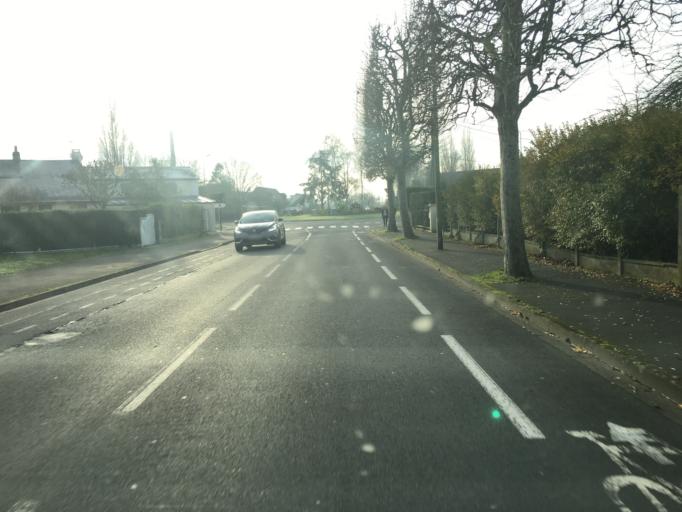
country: FR
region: Lower Normandy
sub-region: Departement du Calvados
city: Cabourg
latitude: 49.2836
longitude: -0.1167
